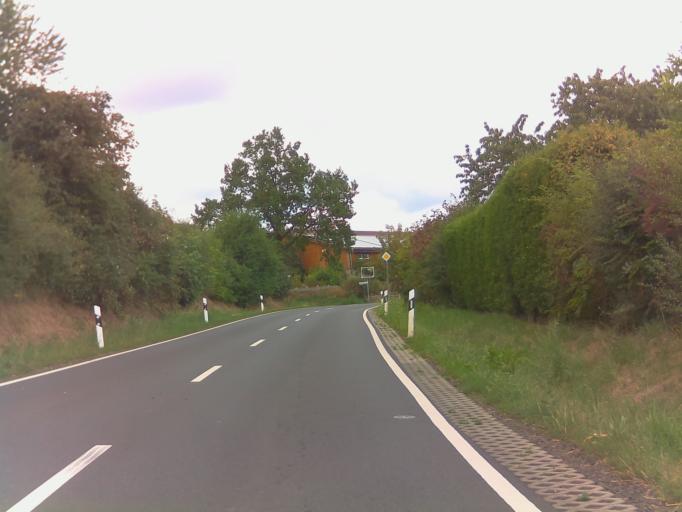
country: DE
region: Hesse
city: Gedern
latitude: 50.3879
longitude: 9.1961
